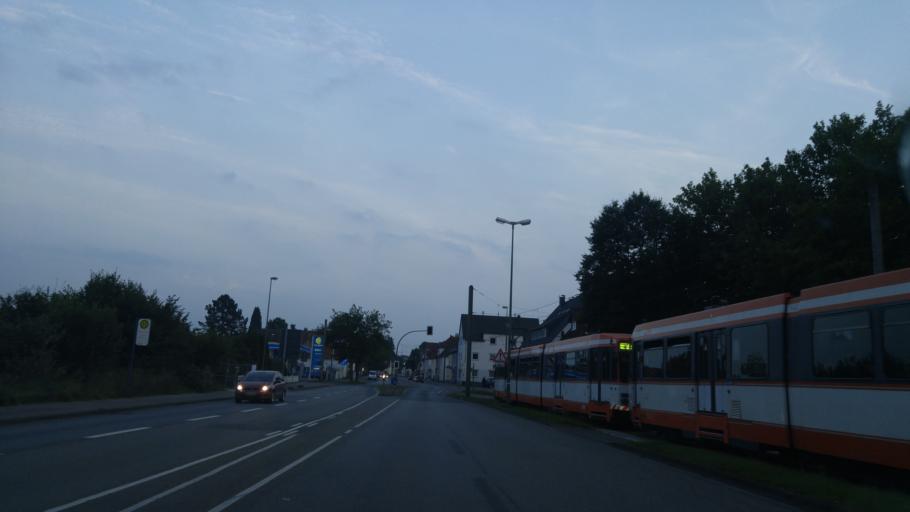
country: DE
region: North Rhine-Westphalia
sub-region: Regierungsbezirk Detmold
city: Bielefeld
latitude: 52.0534
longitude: 8.5193
